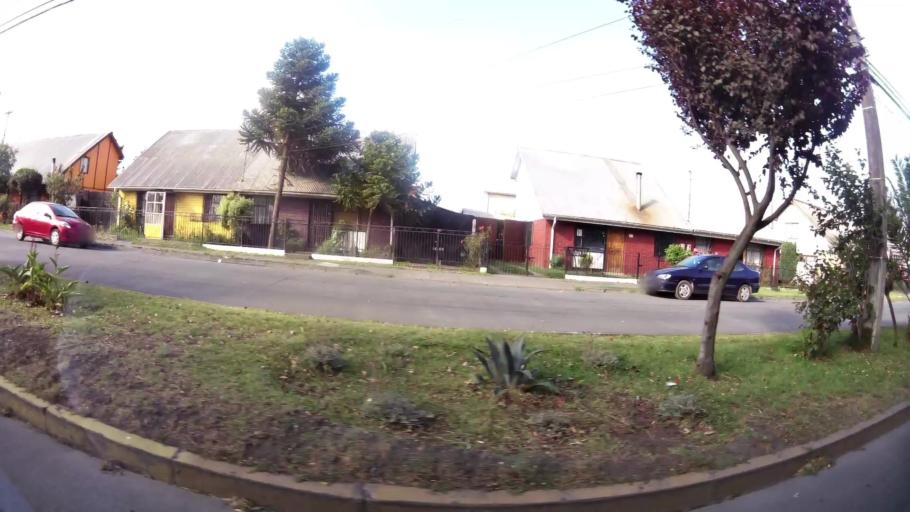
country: CL
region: Biobio
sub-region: Provincia de Concepcion
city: Concepcion
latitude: -36.7993
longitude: -73.0965
